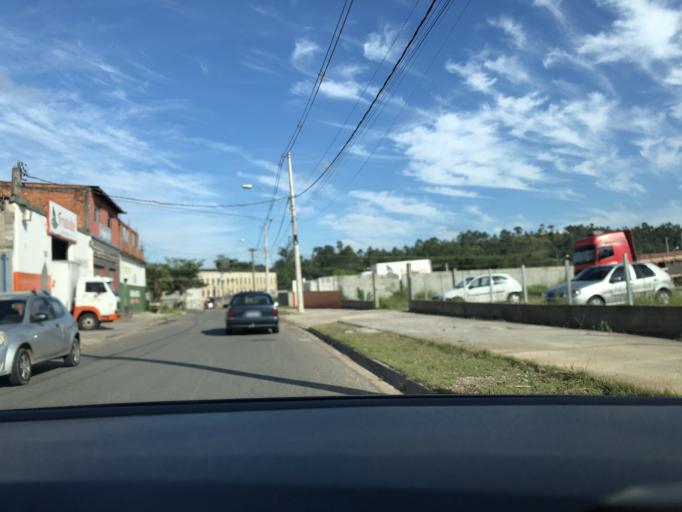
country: BR
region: Sao Paulo
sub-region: Campo Limpo Paulista
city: Campo Limpo Paulista
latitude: -23.2105
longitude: -46.8041
